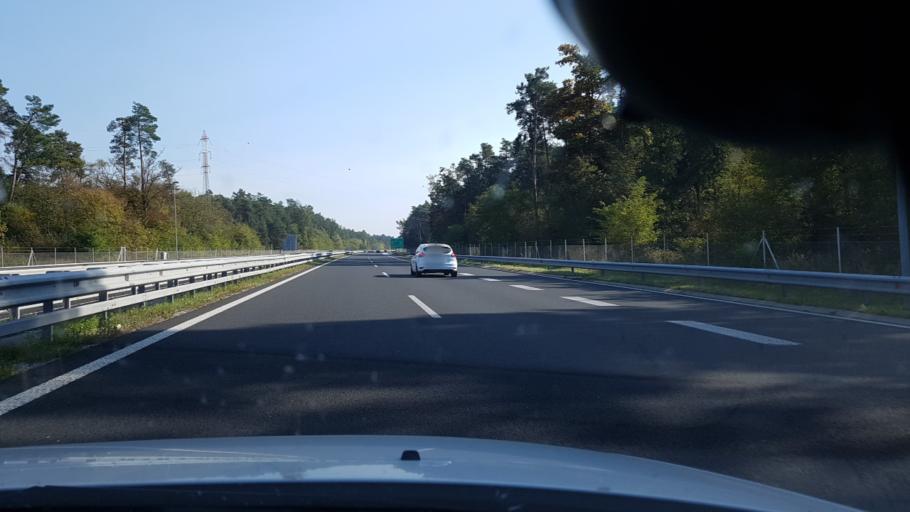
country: SI
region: Starse
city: Starse
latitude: 46.4400
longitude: 15.7831
